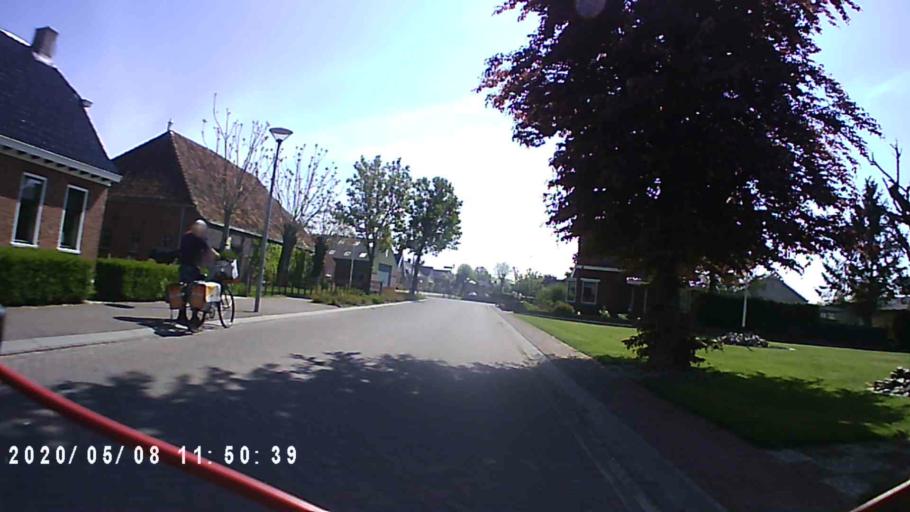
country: NL
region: Groningen
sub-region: Gemeente Bedum
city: Bedum
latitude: 53.3207
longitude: 6.6937
